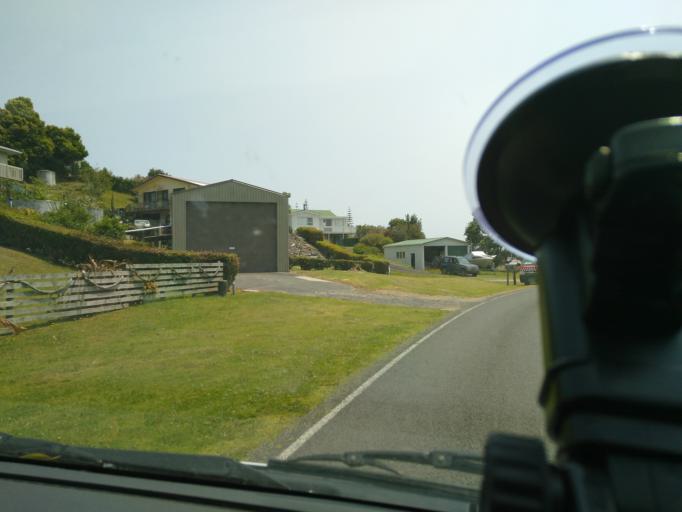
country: NZ
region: Northland
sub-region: Far North District
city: Kaitaia
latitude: -34.8161
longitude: 173.1165
